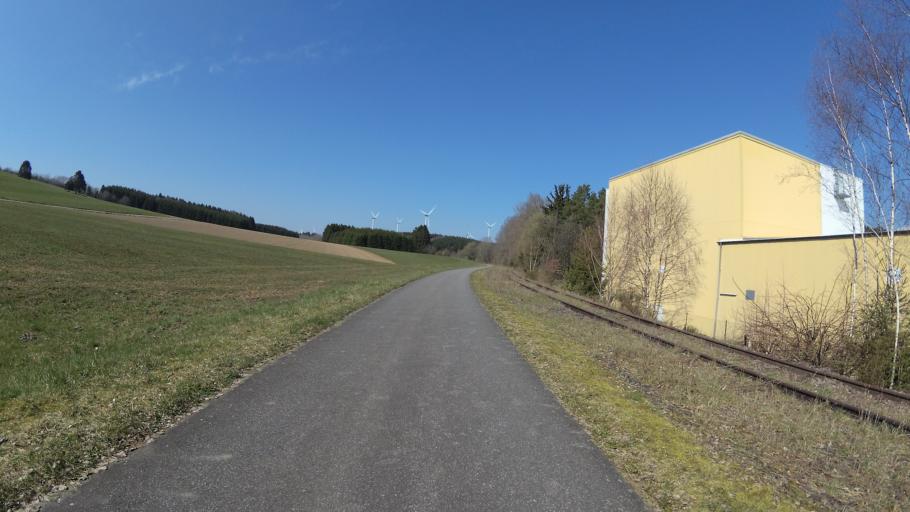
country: DE
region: Rheinland-Pfalz
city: Hermeskeil
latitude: 49.6648
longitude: 6.9298
